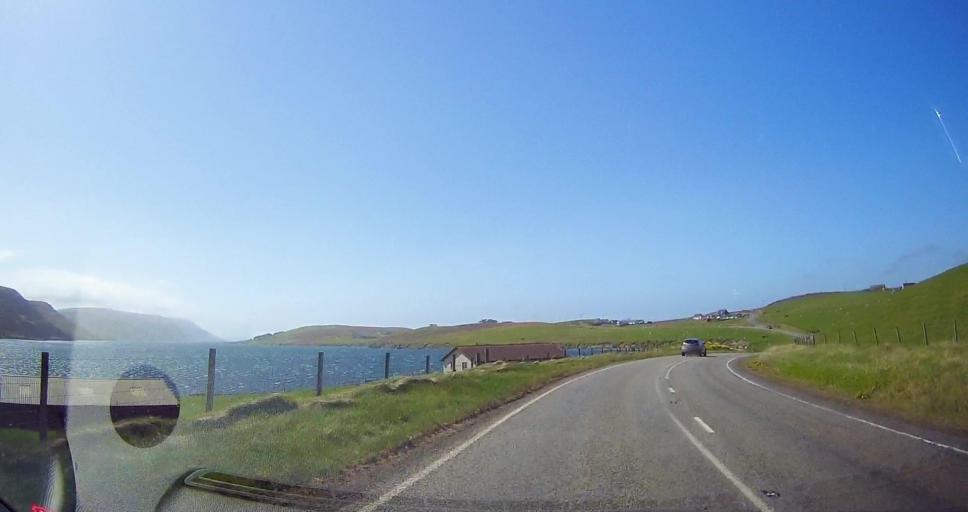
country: GB
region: Scotland
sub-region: Shetland Islands
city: Sandwick
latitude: 60.1274
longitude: -1.2770
